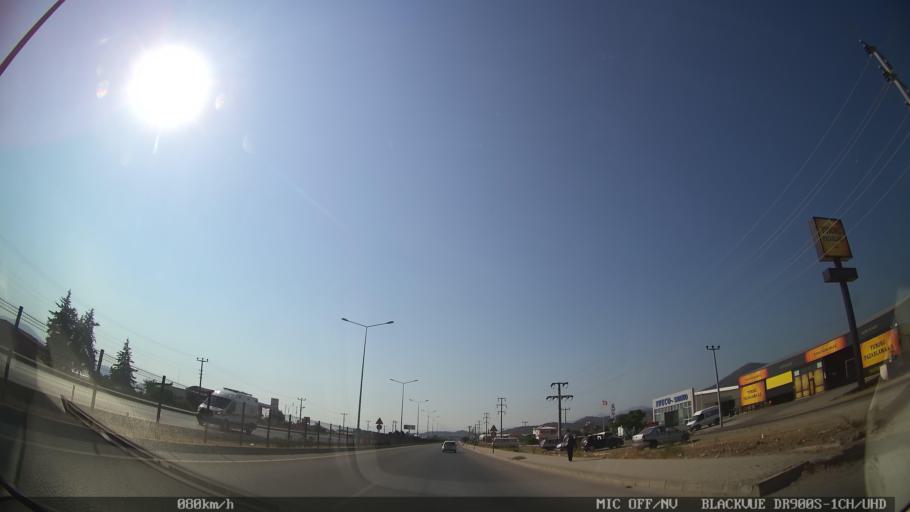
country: TR
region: Mugla
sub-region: Fethiye
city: Fethiye
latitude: 36.6566
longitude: 29.1603
